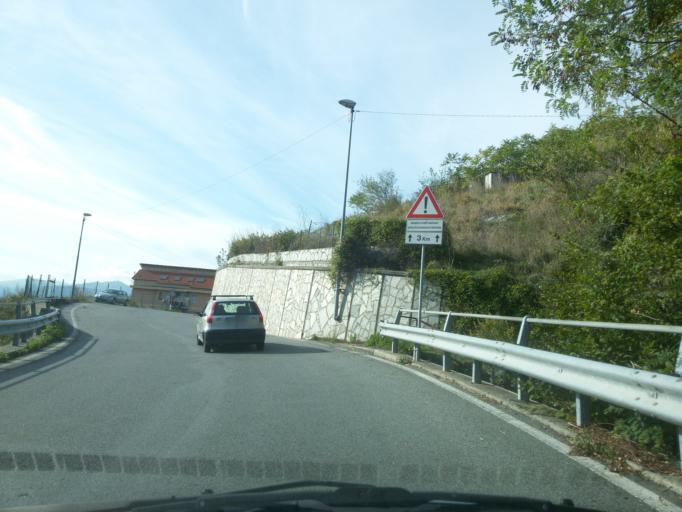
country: IT
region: Liguria
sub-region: Provincia di Genova
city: Piccarello
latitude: 44.4871
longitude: 8.9770
